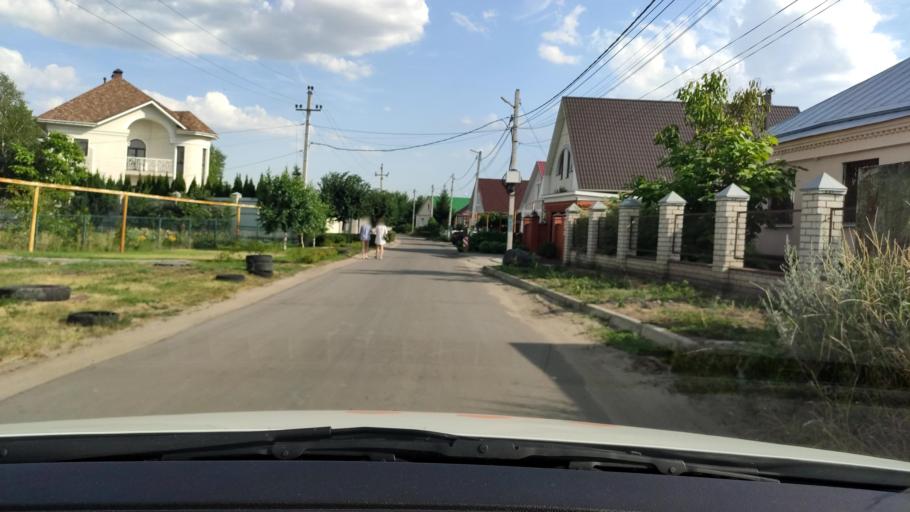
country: RU
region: Voronezj
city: Novaya Usman'
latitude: 51.6320
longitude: 39.4148
